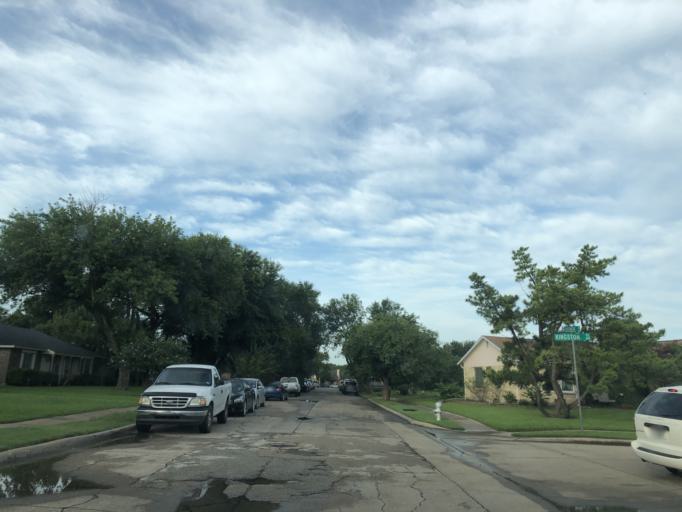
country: US
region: Texas
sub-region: Dallas County
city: Garland
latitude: 32.8475
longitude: -96.6196
